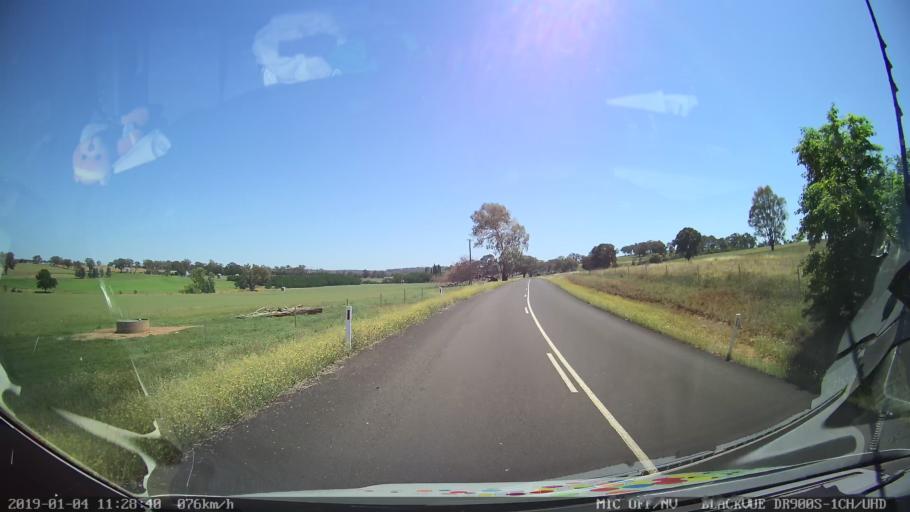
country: AU
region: New South Wales
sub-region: Cabonne
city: Molong
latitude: -33.0972
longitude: 148.7721
